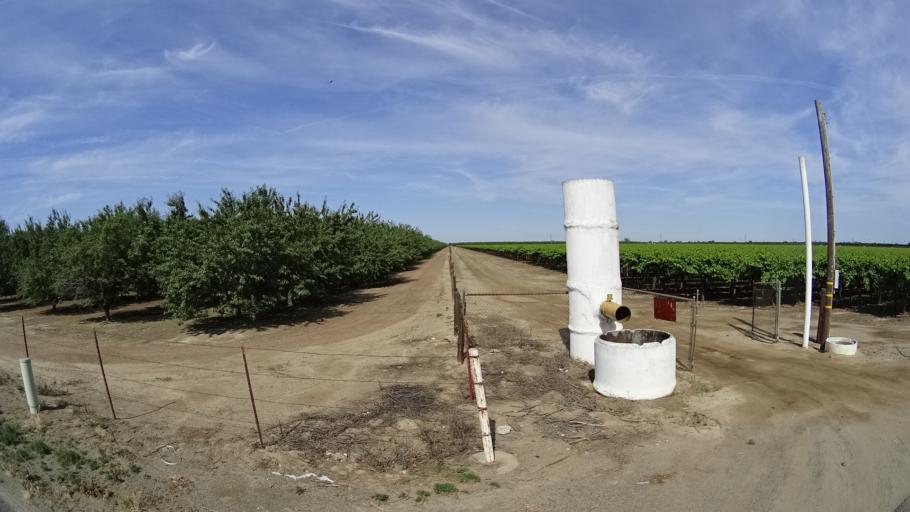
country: US
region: California
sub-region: Kings County
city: Lucerne
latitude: 36.4123
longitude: -119.5829
